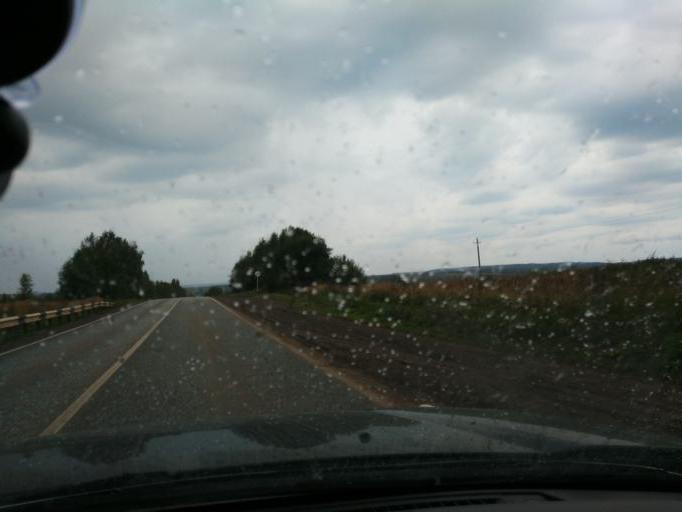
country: RU
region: Perm
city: Chernushka
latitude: 56.8458
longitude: 55.9661
